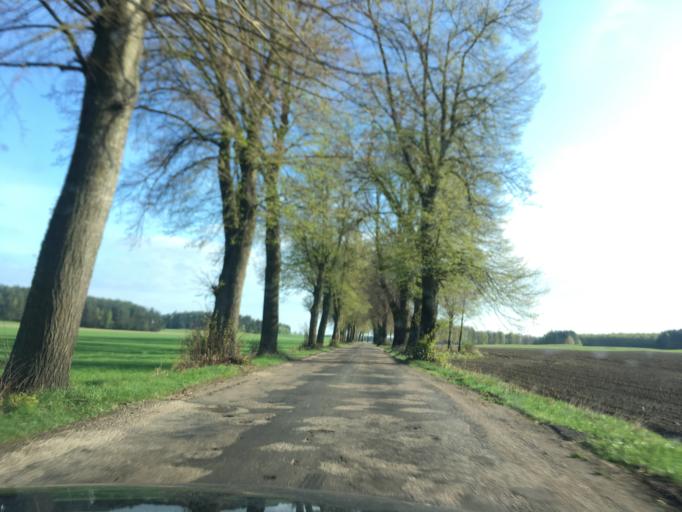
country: PL
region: Warmian-Masurian Voivodeship
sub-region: Powiat nidzicki
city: Nidzica
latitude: 53.4223
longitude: 20.3429
